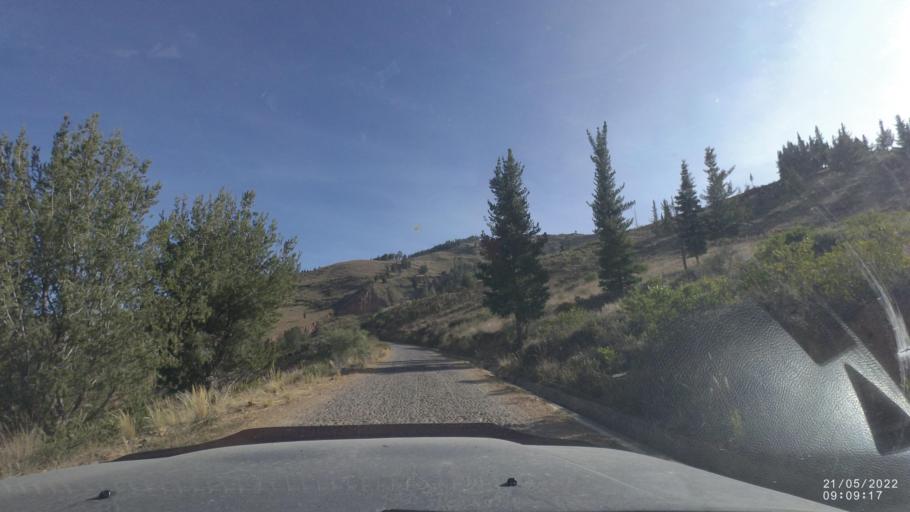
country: BO
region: Cochabamba
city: Cochabamba
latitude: -17.3743
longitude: -66.0242
